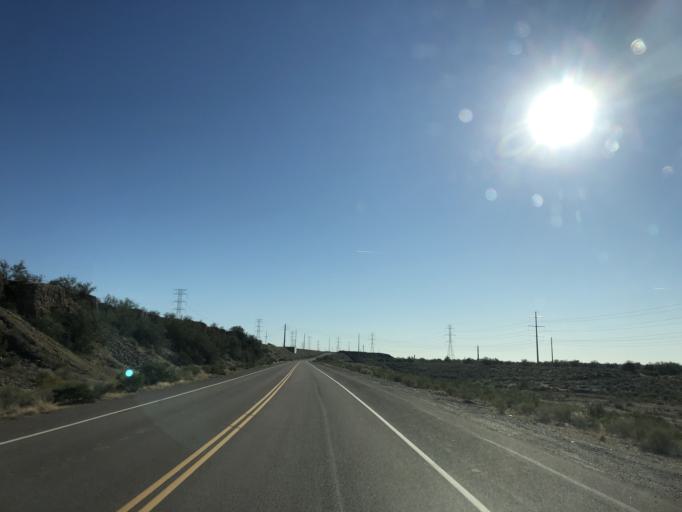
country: US
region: Arizona
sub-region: Maricopa County
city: Sun City West
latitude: 33.6860
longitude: -112.2970
